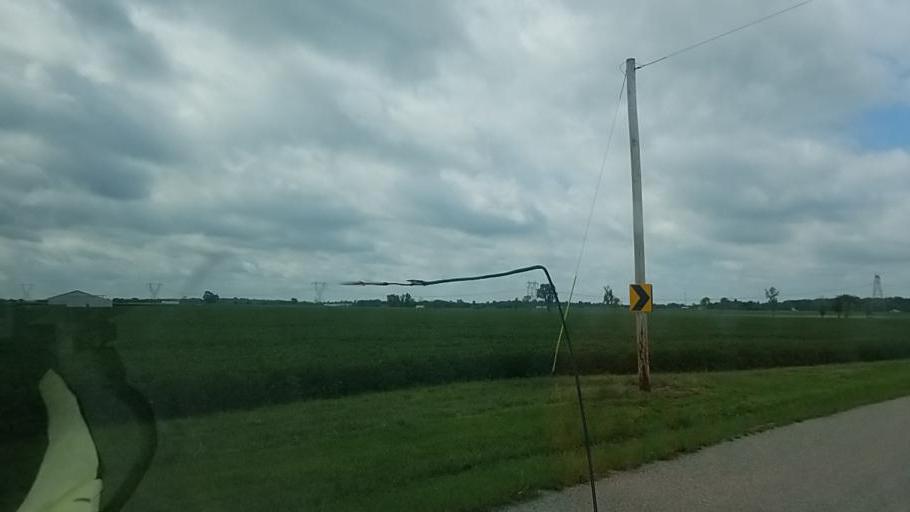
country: US
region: Ohio
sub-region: Madison County
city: Mount Sterling
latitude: 39.7987
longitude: -83.2329
